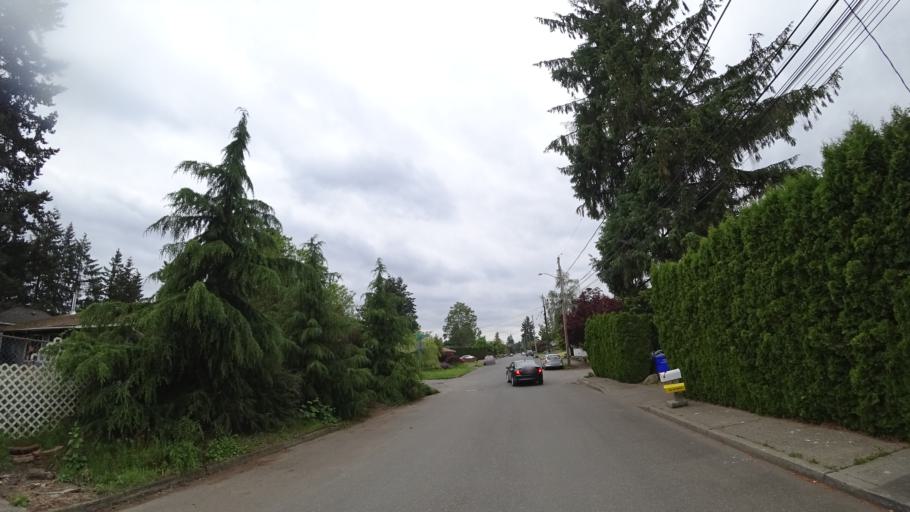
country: US
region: Oregon
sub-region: Multnomah County
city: Lents
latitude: 45.5109
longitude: -122.5322
